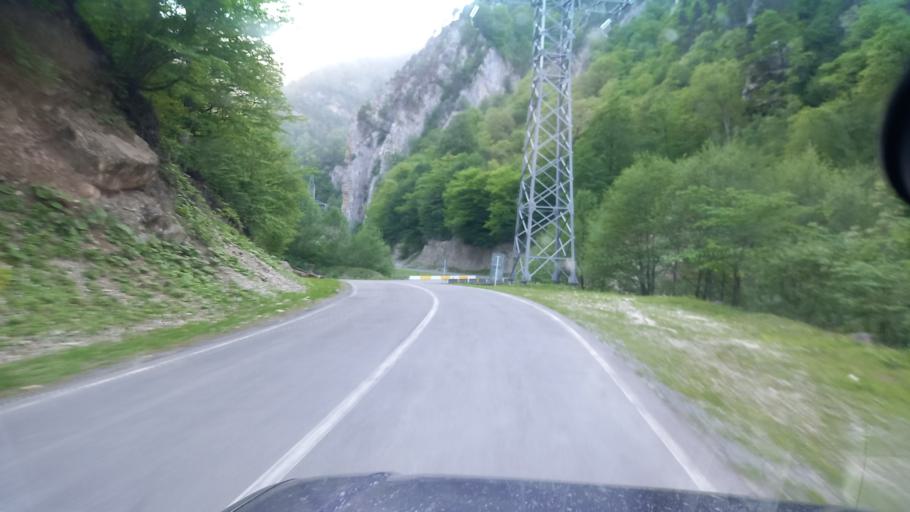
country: RU
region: North Ossetia
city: Tarskoye
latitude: 42.8899
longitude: 44.9389
